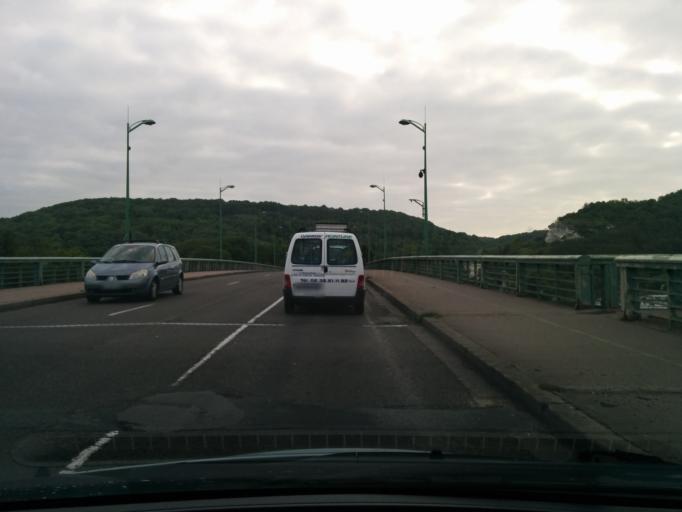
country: FR
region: Haute-Normandie
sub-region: Departement de l'Eure
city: Vernon
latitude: 49.0950
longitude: 1.4868
